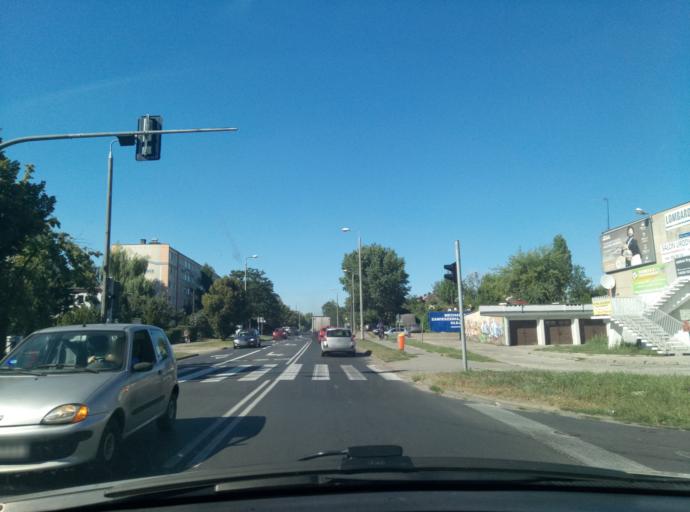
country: PL
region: Kujawsko-Pomorskie
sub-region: Torun
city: Torun
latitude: 53.0286
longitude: 18.6015
